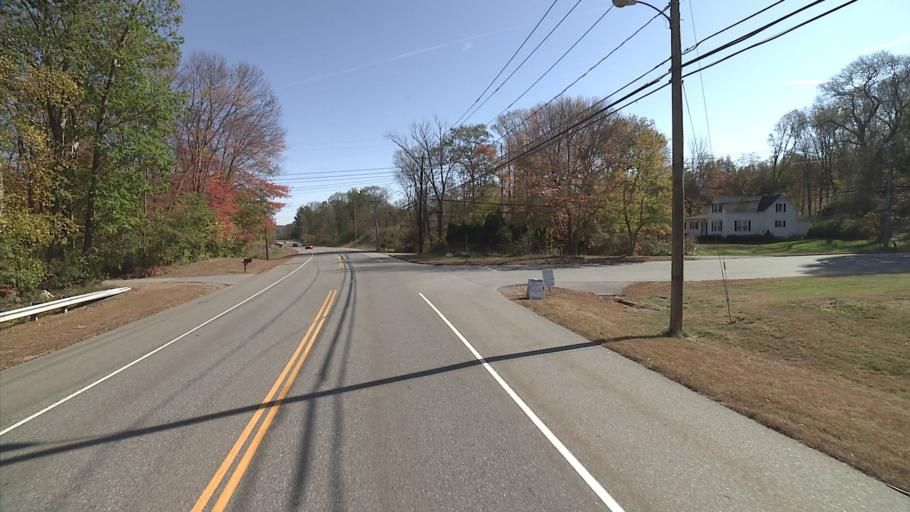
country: US
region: Connecticut
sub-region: Windham County
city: Wauregan
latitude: 41.7824
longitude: -71.9798
